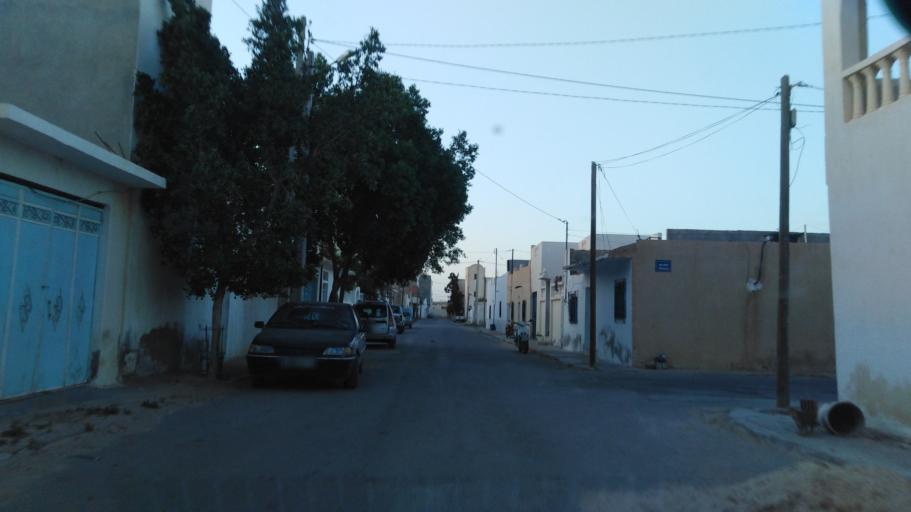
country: TN
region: Tataouine
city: Tataouine
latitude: 32.9361
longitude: 10.4521
